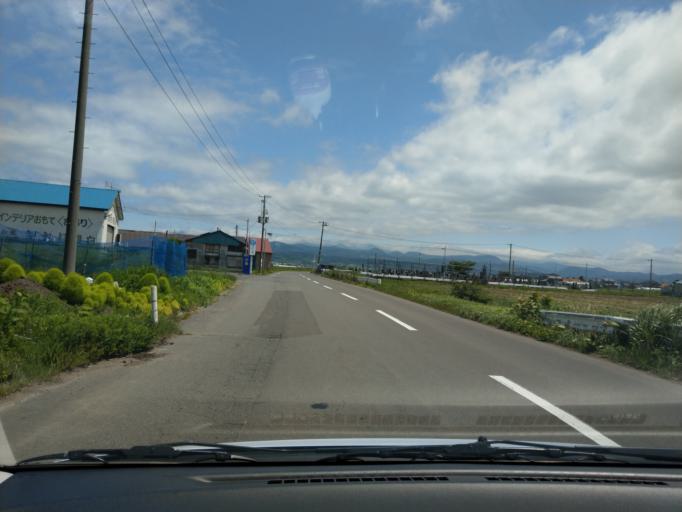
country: JP
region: Aomori
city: Namioka
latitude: 40.6835
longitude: 140.5589
